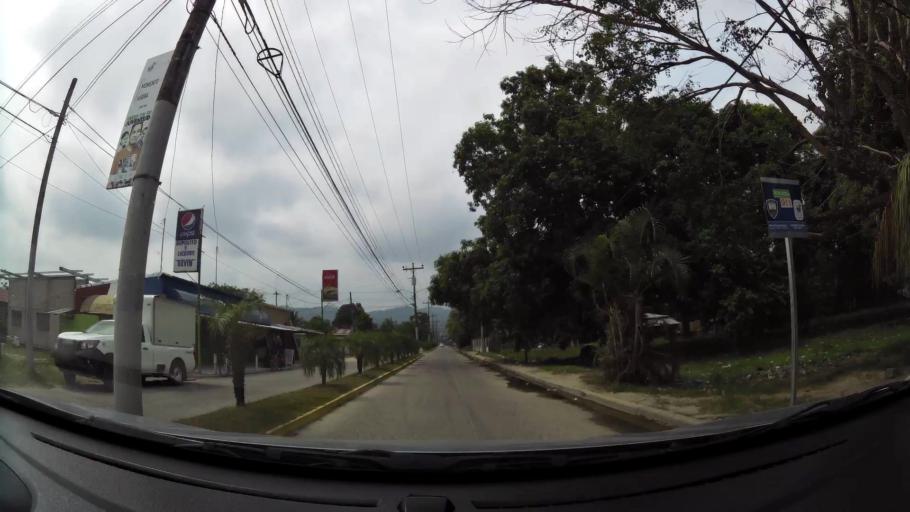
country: HN
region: Atlantida
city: Tela
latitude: 15.7696
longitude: -87.4816
